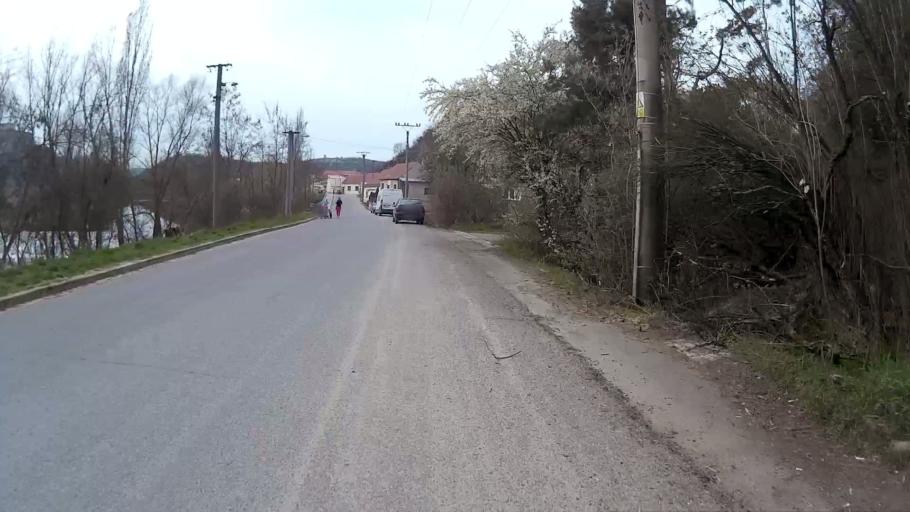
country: CZ
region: South Moravian
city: Dolni Kounice
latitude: 49.0708
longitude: 16.4717
